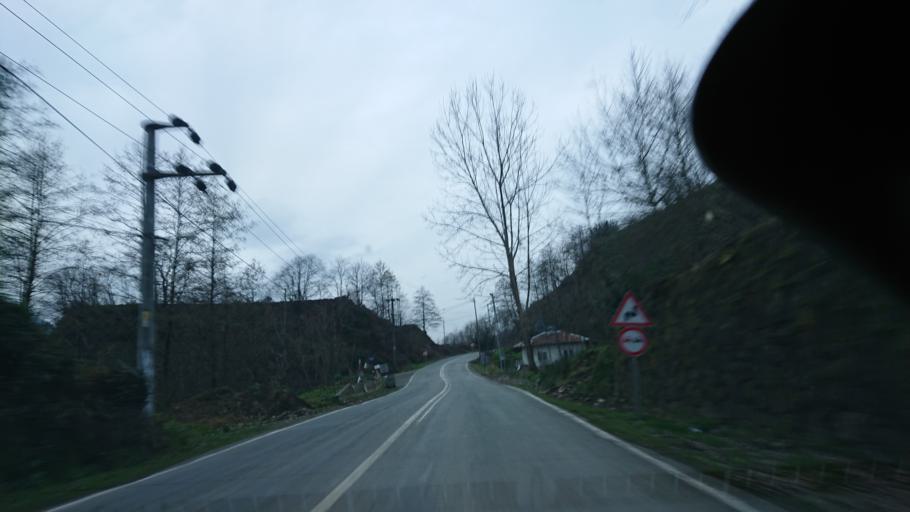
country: TR
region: Rize
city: Rize
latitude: 41.0123
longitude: 40.4922
